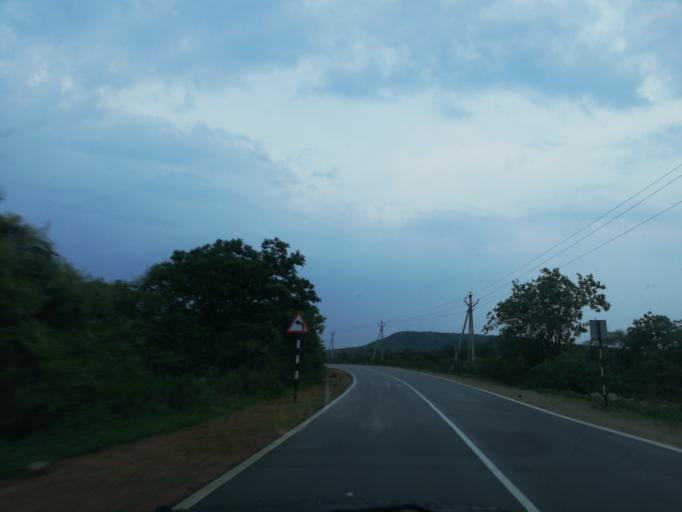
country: IN
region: Andhra Pradesh
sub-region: Guntur
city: Macherla
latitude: 16.6460
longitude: 79.2911
